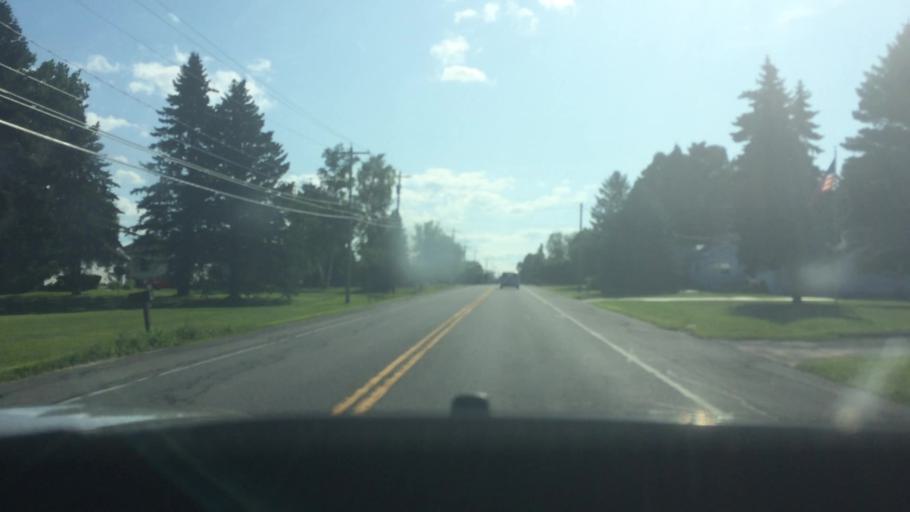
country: US
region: New York
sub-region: Franklin County
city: Malone
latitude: 44.8425
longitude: -74.3058
